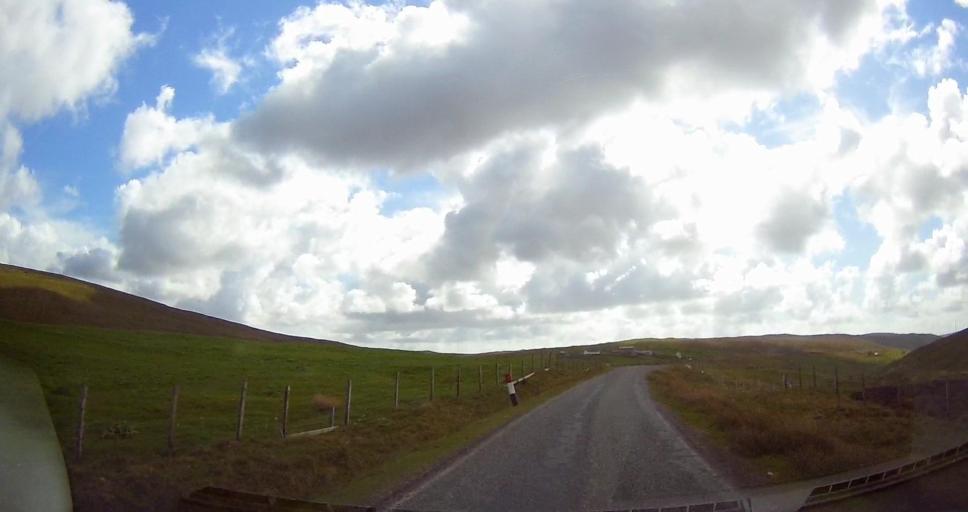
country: GB
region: Scotland
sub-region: Shetland Islands
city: Lerwick
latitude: 60.5148
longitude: -1.3811
